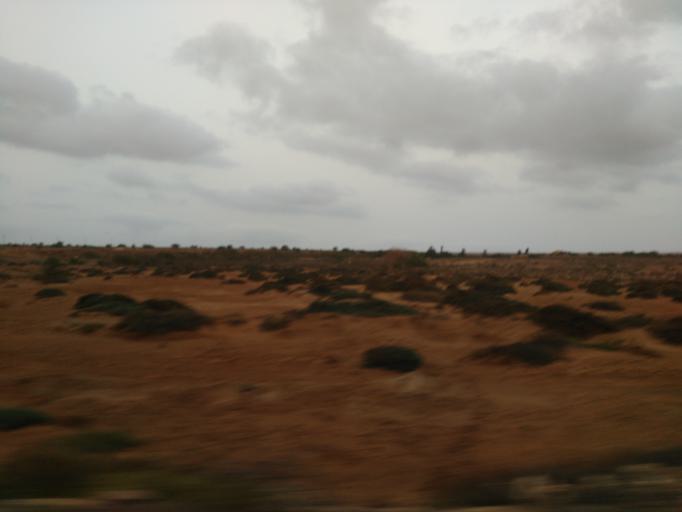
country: CV
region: Sal
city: Espargos
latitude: 16.6769
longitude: -22.9332
